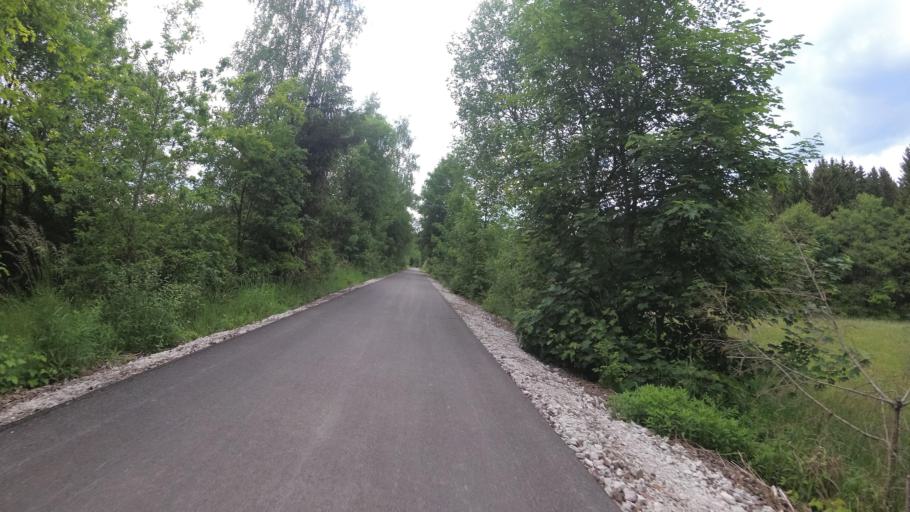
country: DE
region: Rheinland-Pfalz
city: Neuhutten
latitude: 49.6055
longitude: 7.0406
